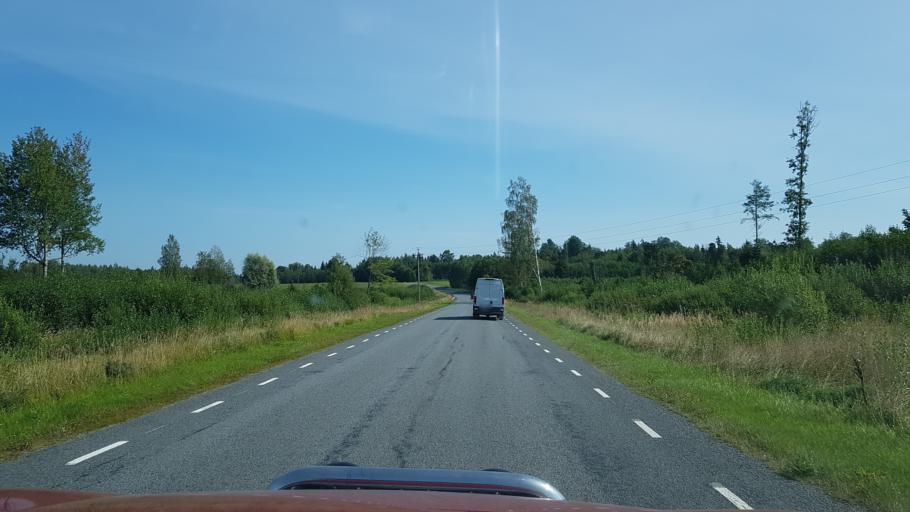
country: EE
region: Viljandimaa
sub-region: Suure-Jaani vald
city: Suure-Jaani
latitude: 58.4962
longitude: 25.5741
